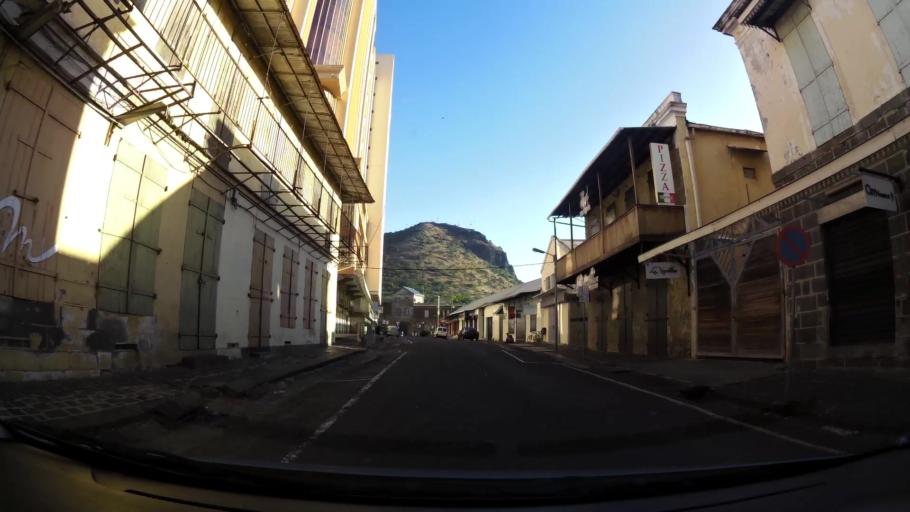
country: MU
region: Port Louis
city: Port Louis
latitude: -20.1644
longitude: 57.5001
